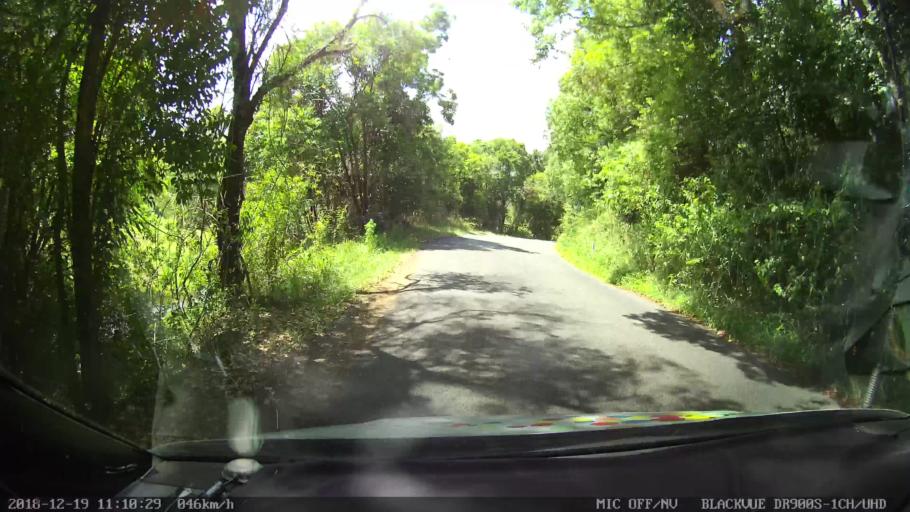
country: AU
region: New South Wales
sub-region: Lismore Municipality
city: Nimbin
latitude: -28.6381
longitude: 153.2600
